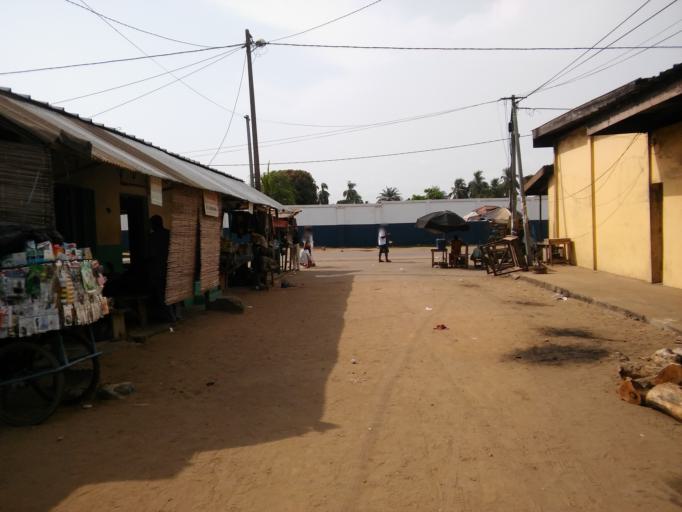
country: CI
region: Sud-Comoe
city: Grand-Bassam
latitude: 5.2074
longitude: -3.7347
